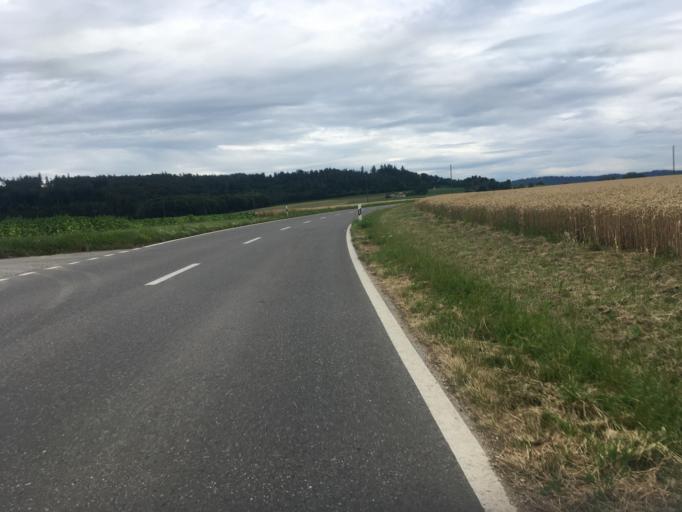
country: CH
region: Bern
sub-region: Seeland District
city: Erlach
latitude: 47.0294
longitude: 7.0956
